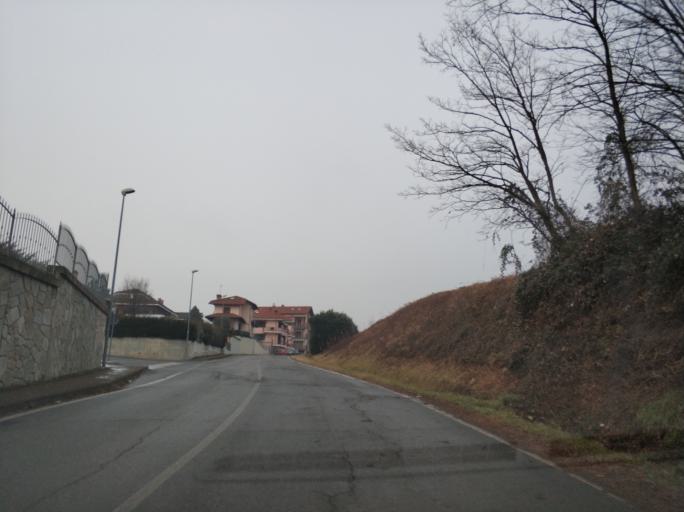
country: IT
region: Piedmont
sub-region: Provincia di Torino
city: San Francesco al Campo
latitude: 45.2230
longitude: 7.6612
